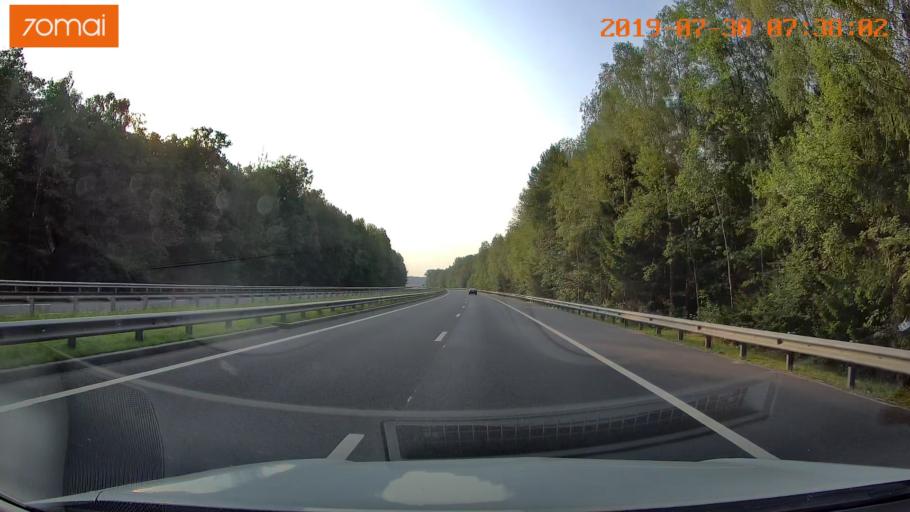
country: RU
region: Kaliningrad
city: Gvardeysk
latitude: 54.6518
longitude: 21.1579
